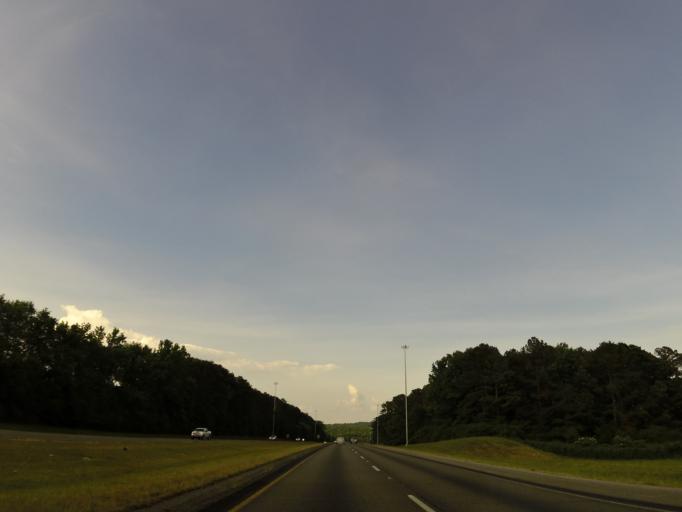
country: US
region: Alabama
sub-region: Jefferson County
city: Trussville
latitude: 33.6512
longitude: -86.6047
